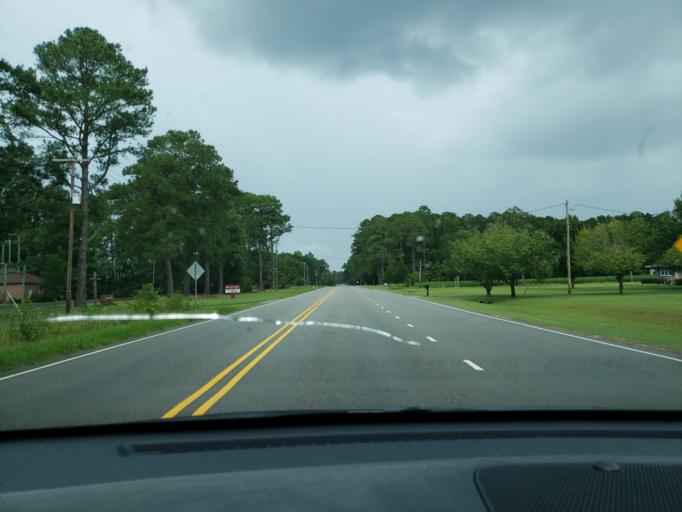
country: US
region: North Carolina
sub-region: Bladen County
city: Elizabethtown
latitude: 34.5049
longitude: -78.6547
